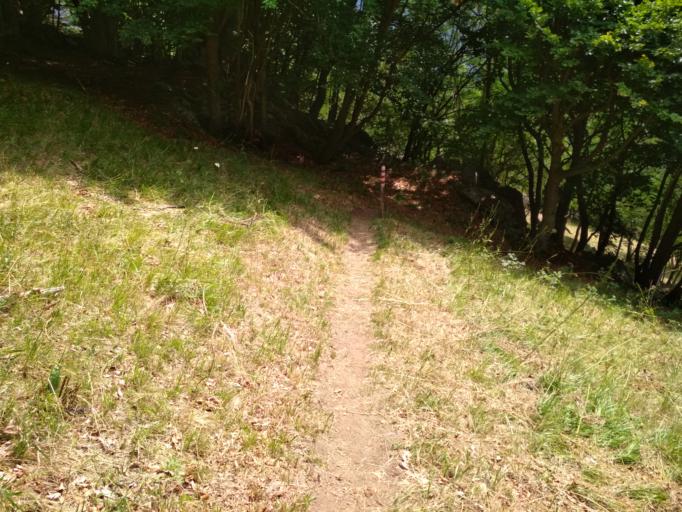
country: IT
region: Piedmont
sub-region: Provincia di Torino
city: Balme
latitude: 45.3045
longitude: 7.2157
